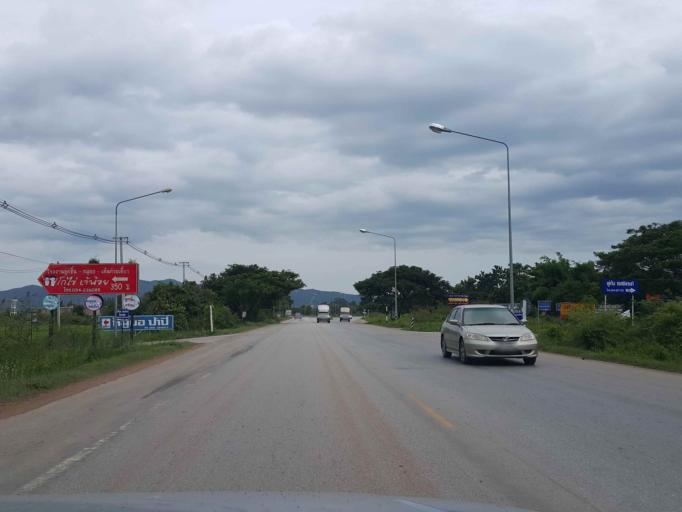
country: TH
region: Lampang
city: Lampang
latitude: 18.2575
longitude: 99.4786
